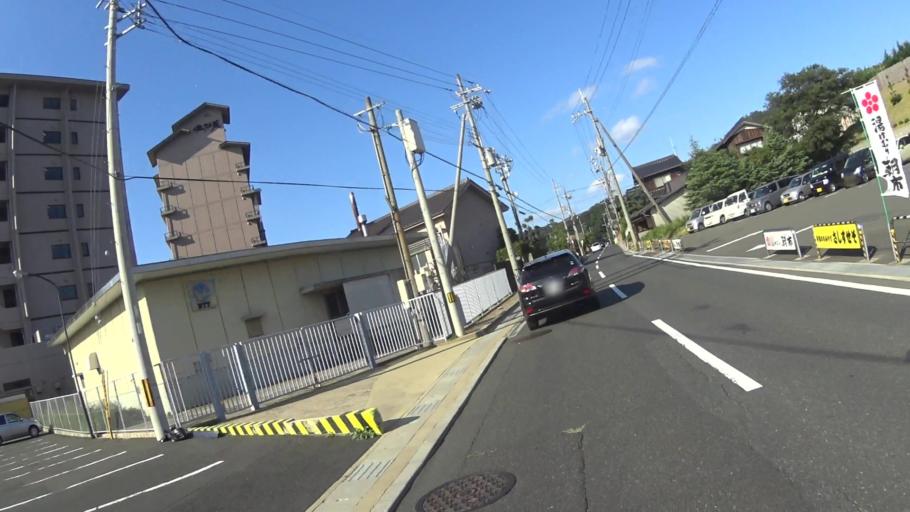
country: JP
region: Hyogo
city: Toyooka
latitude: 35.6588
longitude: 134.9673
